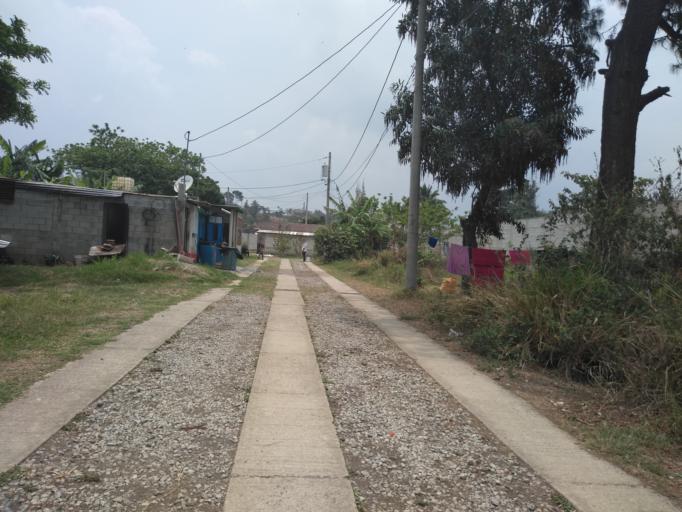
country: GT
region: Guatemala
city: Petapa
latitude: 14.5015
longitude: -90.5537
